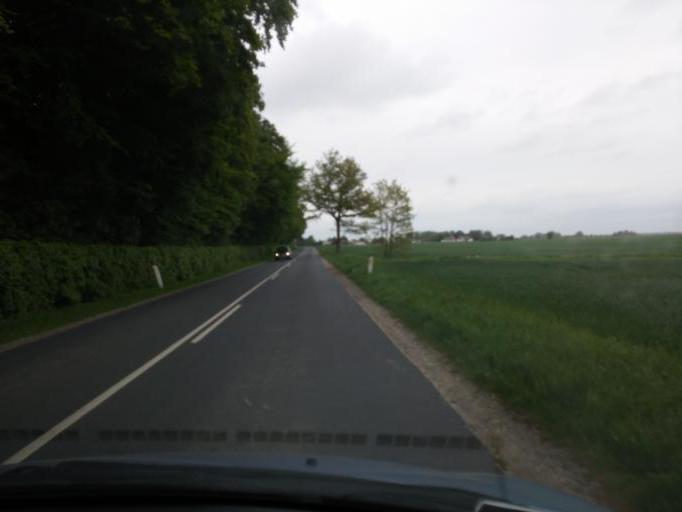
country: DK
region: South Denmark
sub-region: Kerteminde Kommune
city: Kerteminde
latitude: 55.4238
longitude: 10.6152
